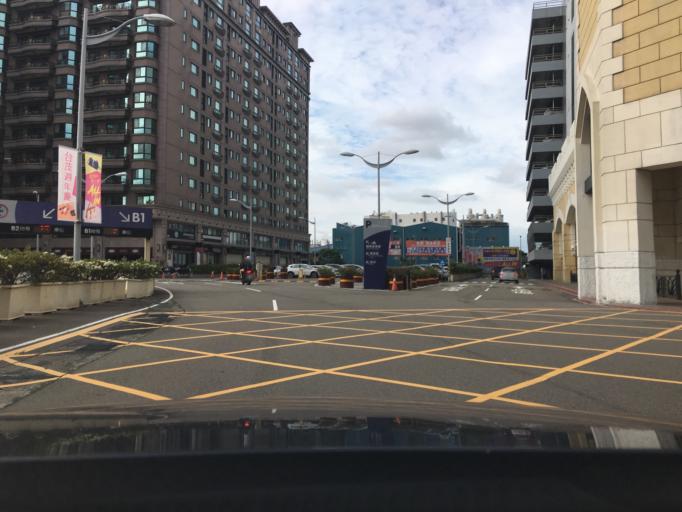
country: TW
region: Taiwan
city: Taoyuan City
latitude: 25.0529
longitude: 121.2877
